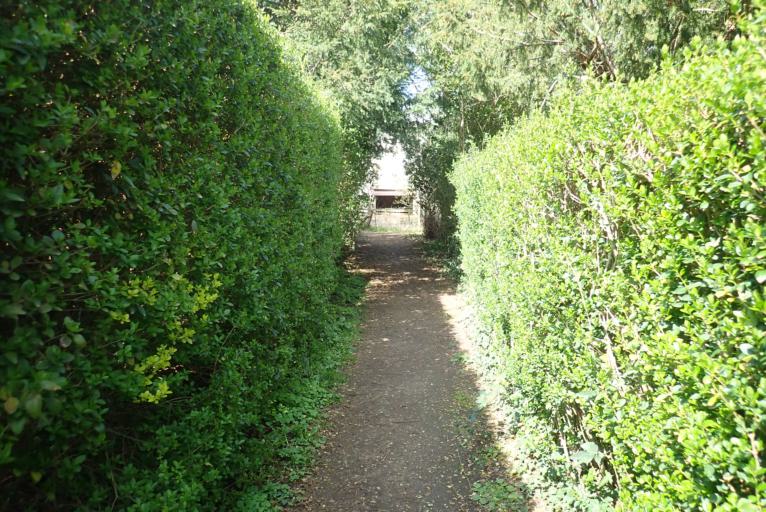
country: BE
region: Flanders
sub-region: Provincie Antwerpen
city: Edegem
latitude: 51.1688
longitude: 4.4080
